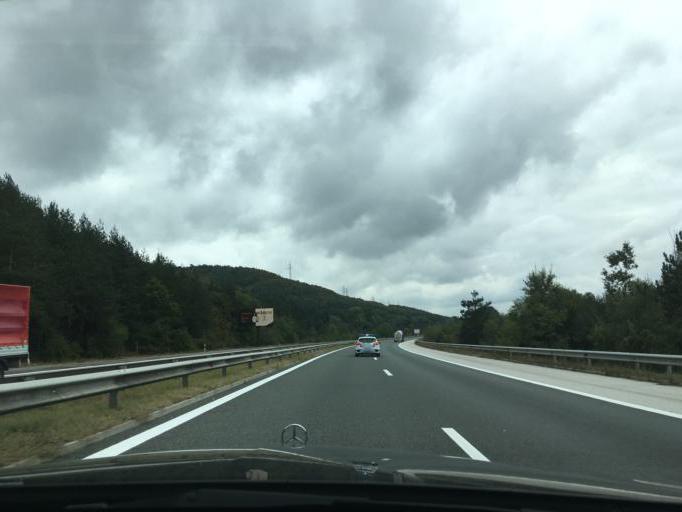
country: BG
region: Sofiya
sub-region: Obshtina Ikhtiman
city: Ikhtiman
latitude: 42.5088
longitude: 23.7629
